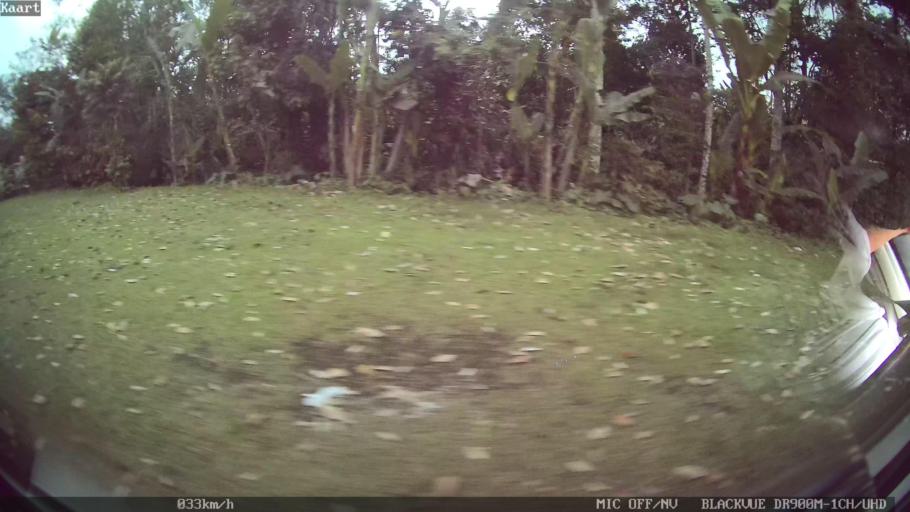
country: ID
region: Bali
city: Petang
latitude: -8.4171
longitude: 115.2253
